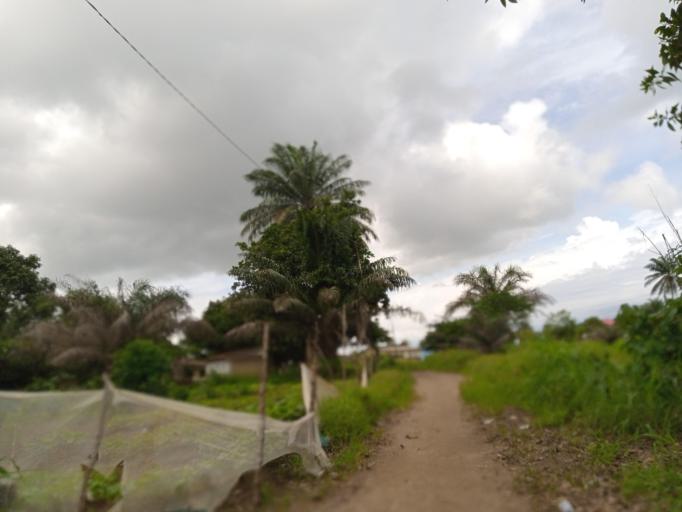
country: SL
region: Northern Province
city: Masoyila
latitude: 8.5882
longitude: -13.1674
